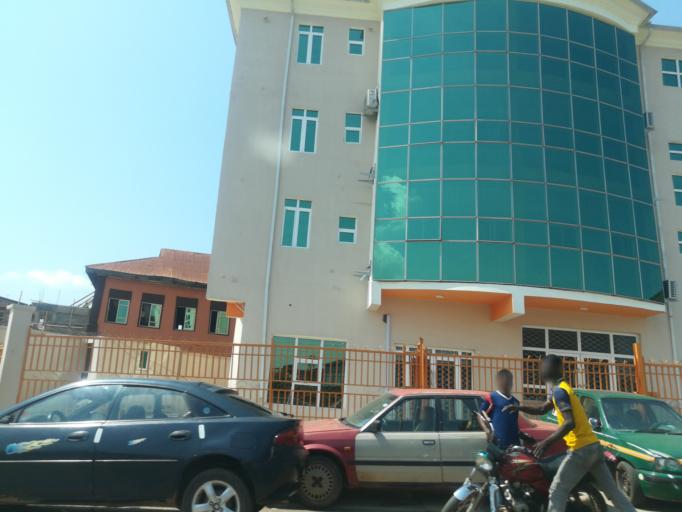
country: NG
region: Ogun
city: Abeokuta
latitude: 7.1485
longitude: 3.3431
